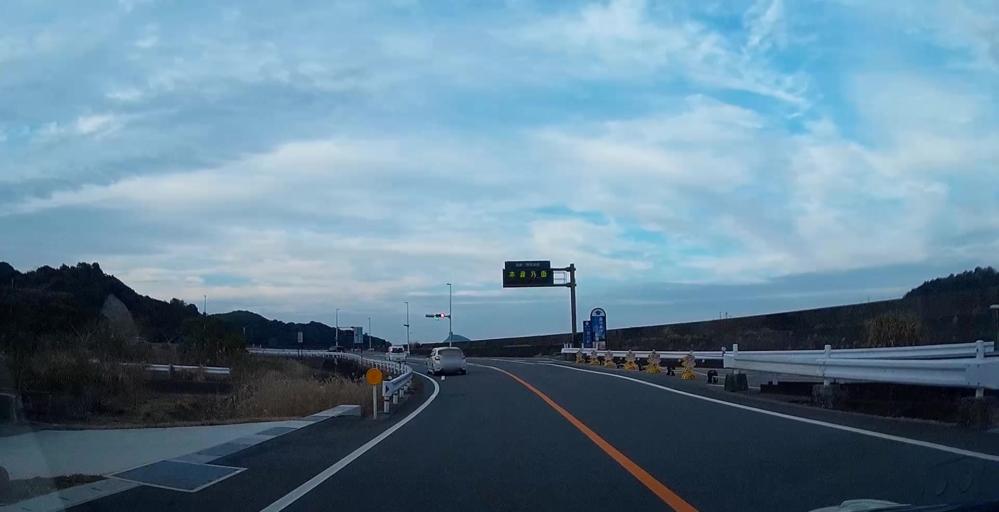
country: JP
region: Kumamoto
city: Hondo
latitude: 32.4988
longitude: 130.3928
